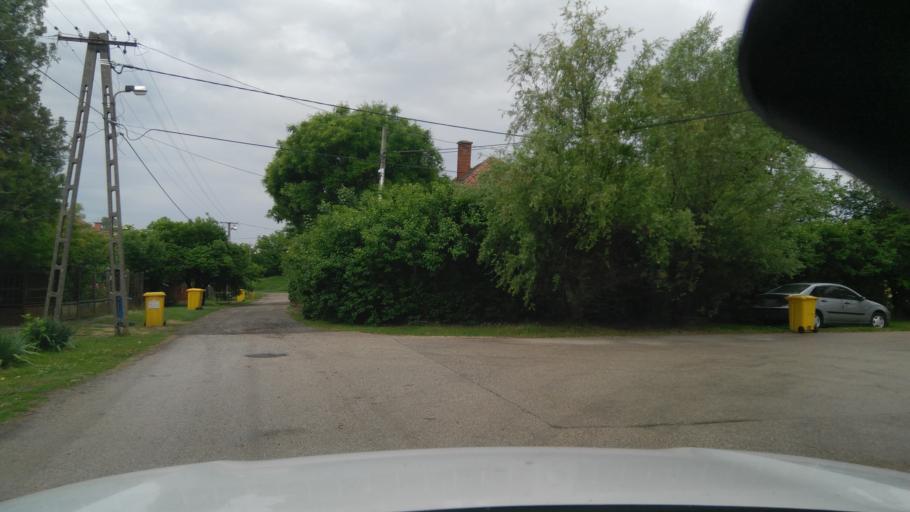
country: HU
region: Bekes
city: Doboz
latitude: 46.6971
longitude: 21.1819
